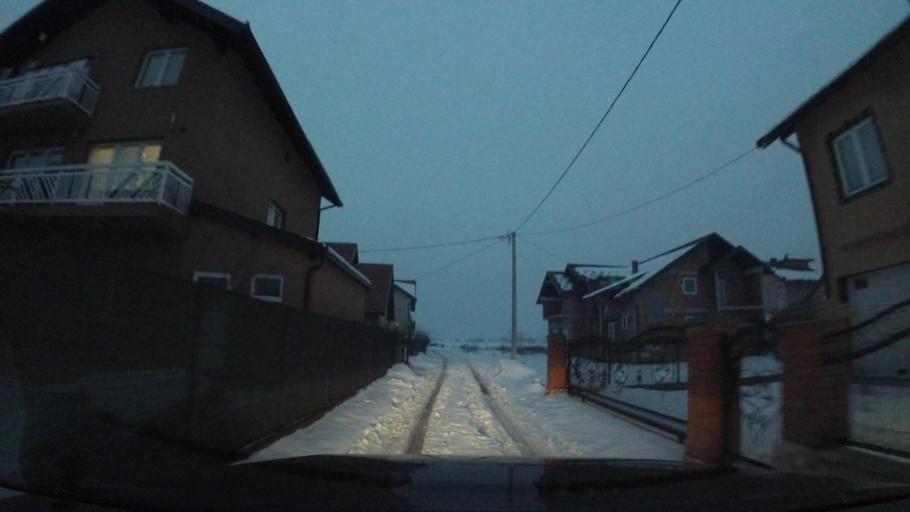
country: BA
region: Federation of Bosnia and Herzegovina
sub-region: Kanton Sarajevo
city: Sarajevo
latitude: 43.8573
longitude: 18.2918
